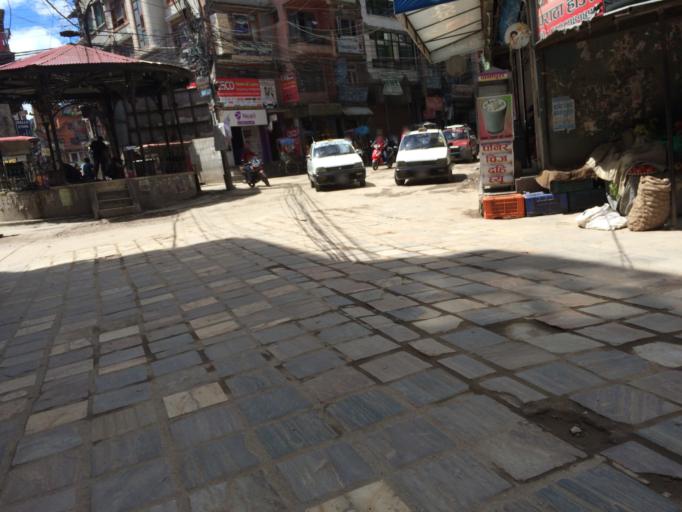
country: NP
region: Central Region
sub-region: Bagmati Zone
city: Kathmandu
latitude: 27.7112
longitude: 85.3088
